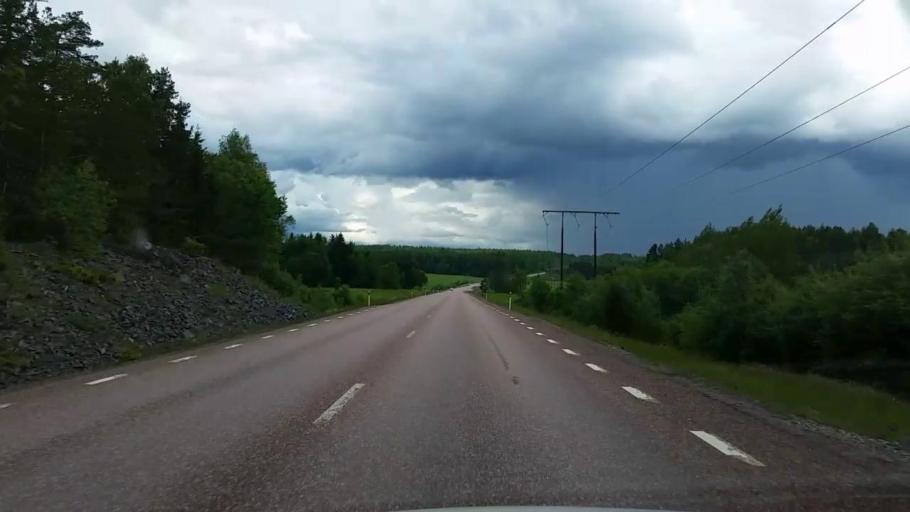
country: SE
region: Gaevleborg
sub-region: Hofors Kommun
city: Hofors
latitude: 60.5337
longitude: 16.4584
